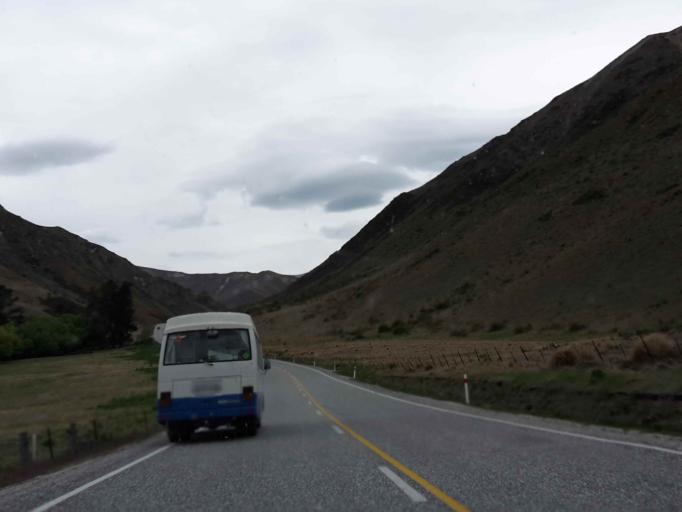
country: NZ
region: Otago
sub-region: Queenstown-Lakes District
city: Wanaka
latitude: -44.5848
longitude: 169.5863
